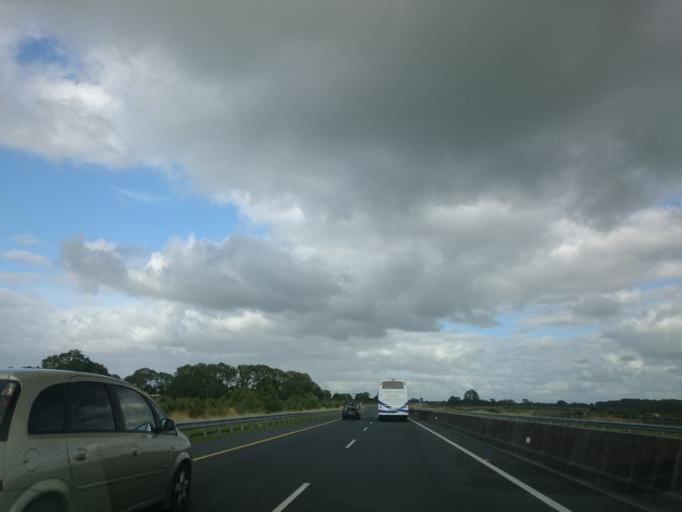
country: IE
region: Connaught
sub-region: County Galway
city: Athenry
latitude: 53.2699
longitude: -8.6614
